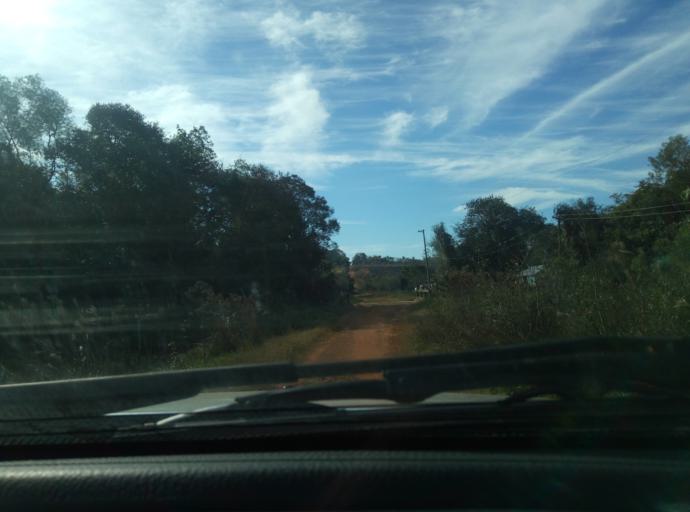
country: PY
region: Caaguazu
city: Carayao
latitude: -25.1668
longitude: -56.2929
